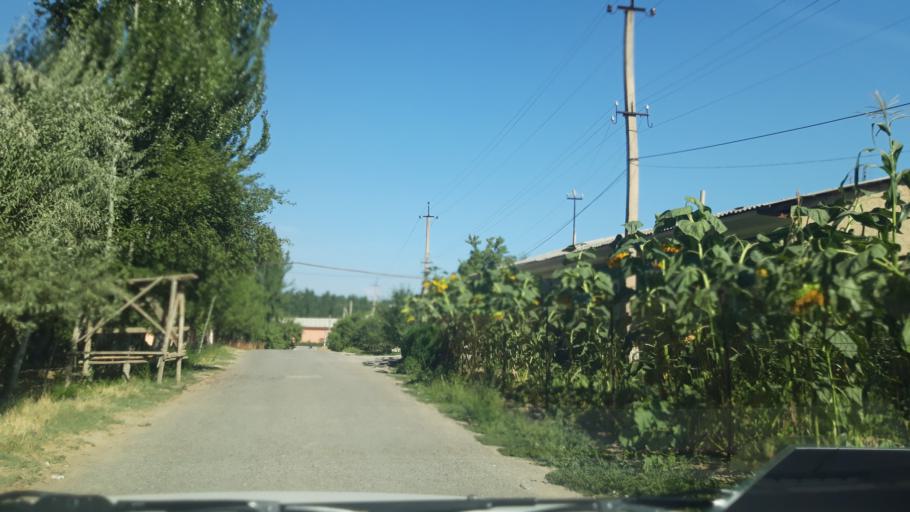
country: UZ
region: Namangan
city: Yangiqo`rg`on
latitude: 41.2025
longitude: 71.7234
